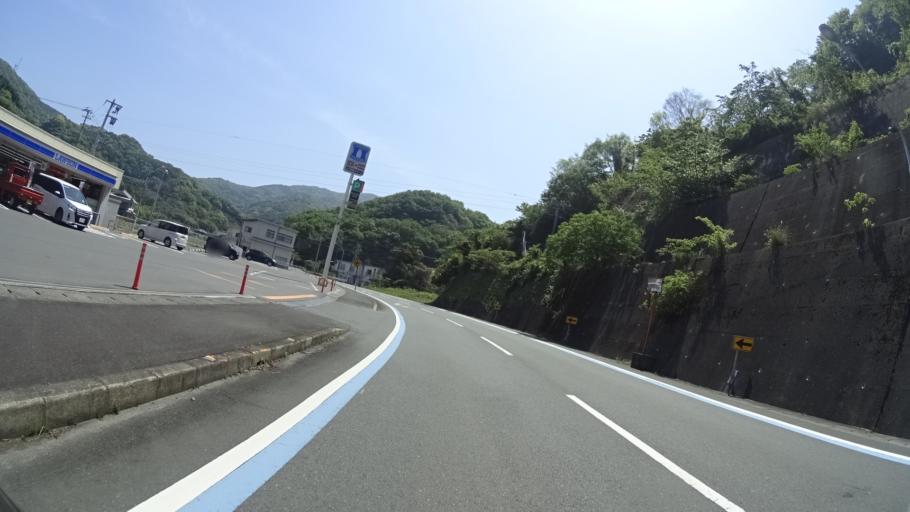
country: JP
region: Ehime
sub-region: Nishiuwa-gun
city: Ikata-cho
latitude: 33.3864
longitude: 132.1257
